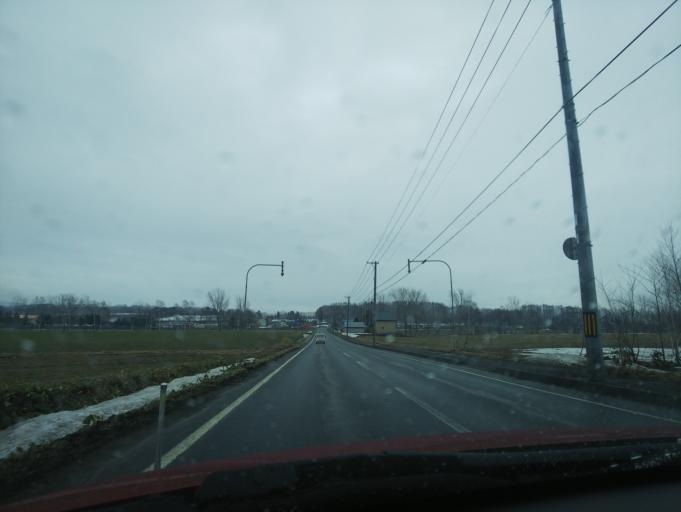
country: JP
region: Hokkaido
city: Nayoro
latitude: 44.3363
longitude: 142.4707
